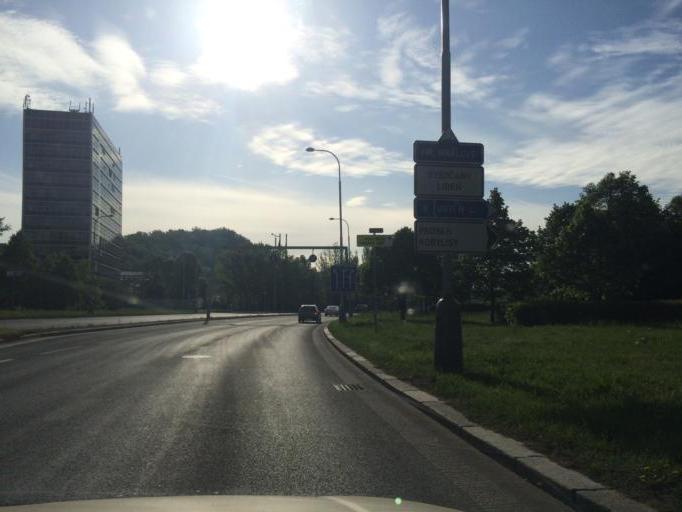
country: CZ
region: Praha
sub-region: Praha 8
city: Karlin
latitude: 50.1150
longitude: 14.4462
